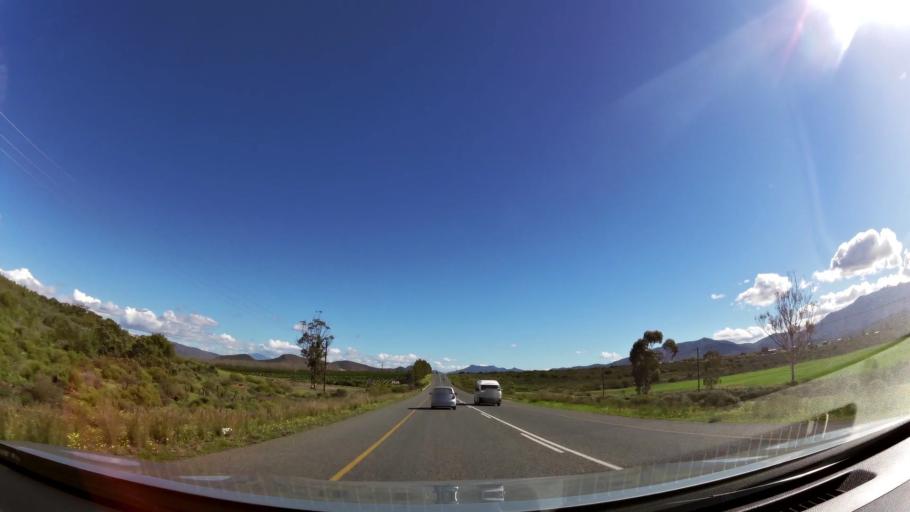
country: ZA
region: Western Cape
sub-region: Cape Winelands District Municipality
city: Ashton
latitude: -33.8142
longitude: 19.9302
